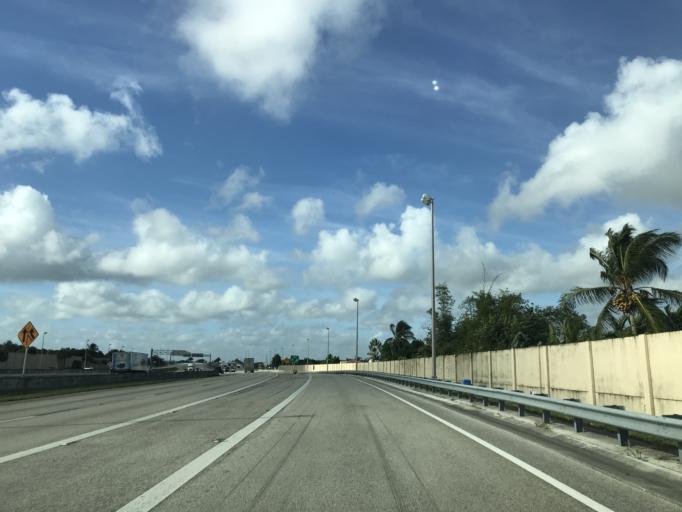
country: US
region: Florida
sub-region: Palm Beach County
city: Boca Pointe
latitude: 26.3052
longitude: -80.1792
